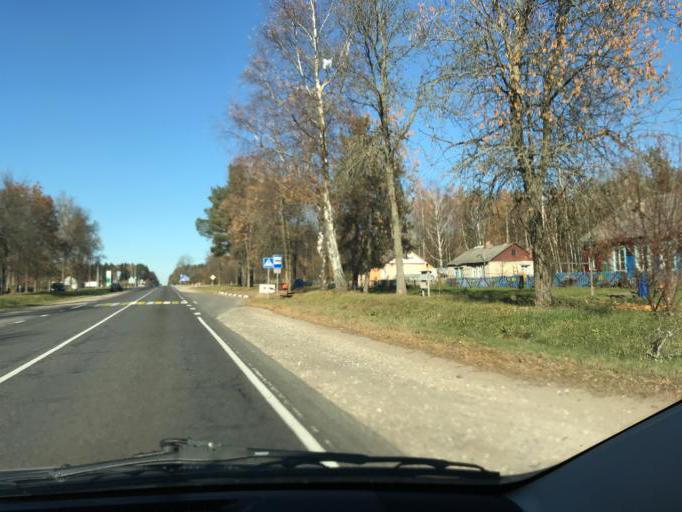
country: BY
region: Vitebsk
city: Polatsk
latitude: 55.5357
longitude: 28.7183
